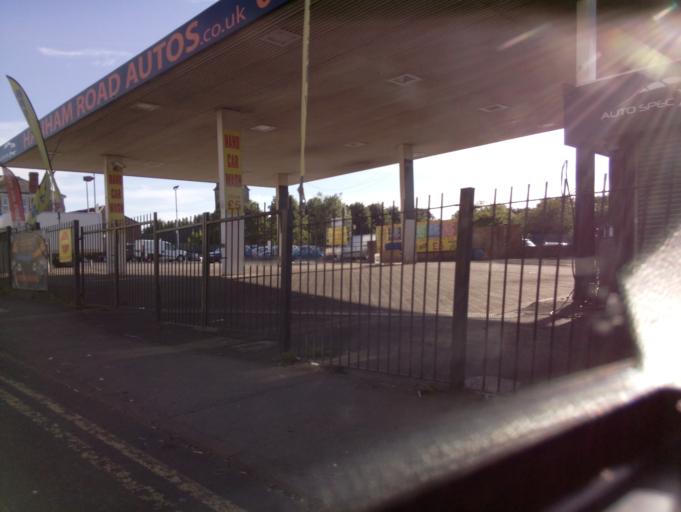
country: GB
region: England
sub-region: South Gloucestershire
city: Kingswood
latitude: 51.4609
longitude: -2.5053
